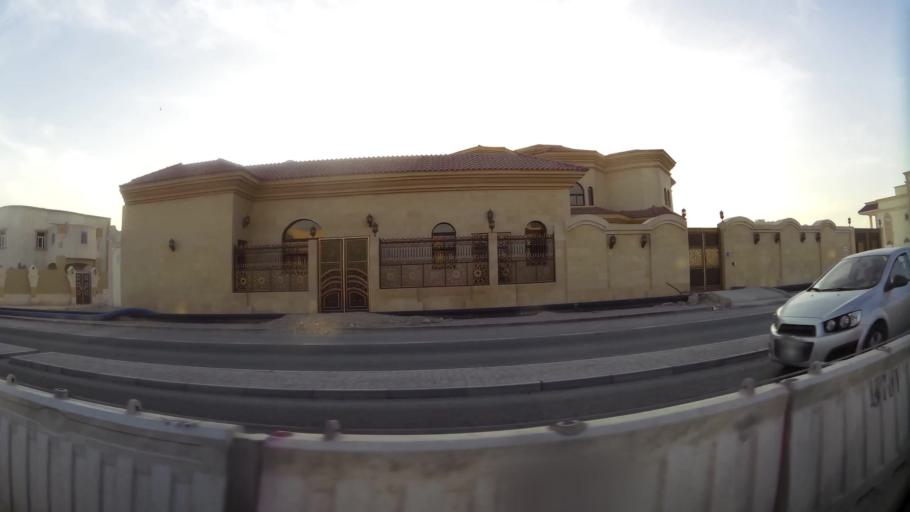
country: QA
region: Al Wakrah
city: Al Wakrah
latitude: 25.1615
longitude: 51.5906
